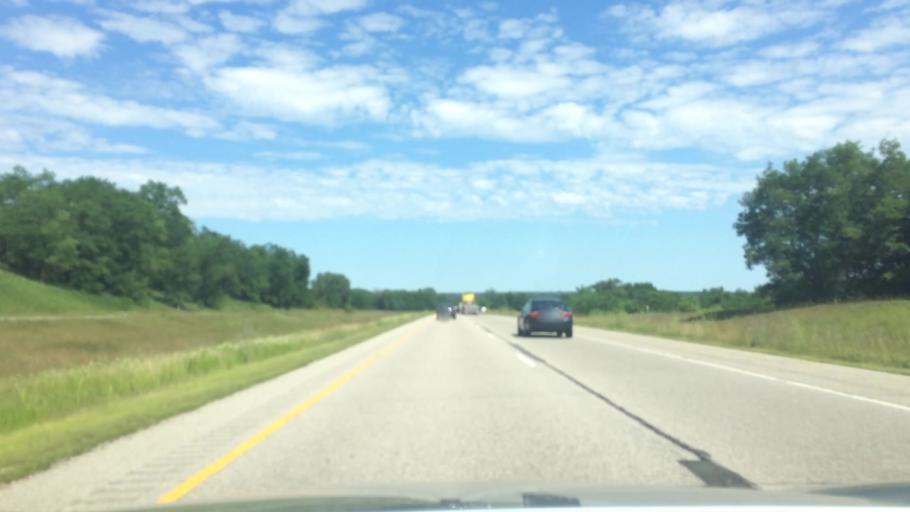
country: US
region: Wisconsin
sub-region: Marquette County
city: Westfield
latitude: 43.7275
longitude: -89.4825
